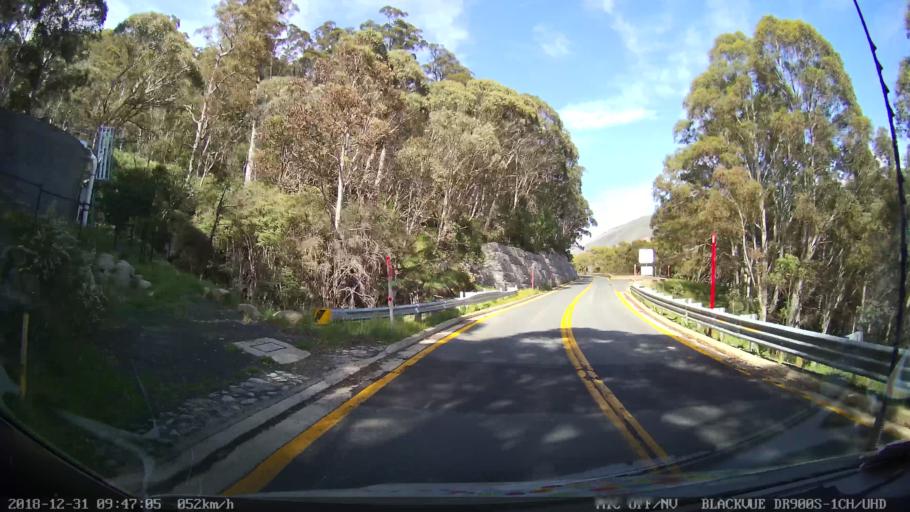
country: AU
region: New South Wales
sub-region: Snowy River
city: Jindabyne
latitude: -36.5072
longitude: 148.3045
